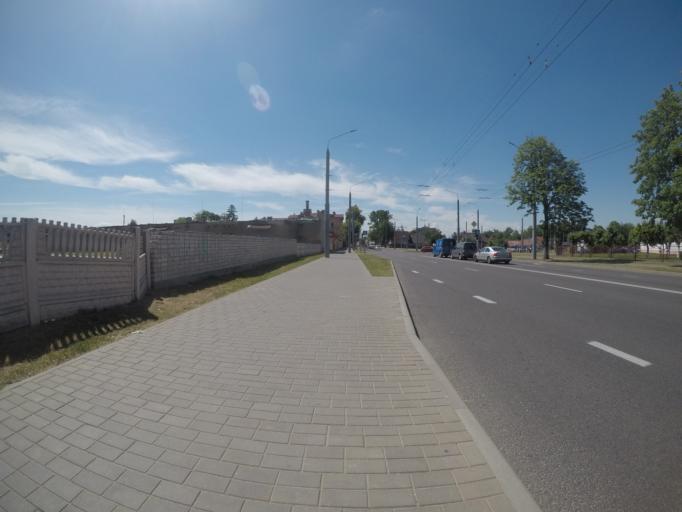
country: BY
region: Grodnenskaya
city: Hrodna
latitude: 53.6915
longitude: 23.8374
